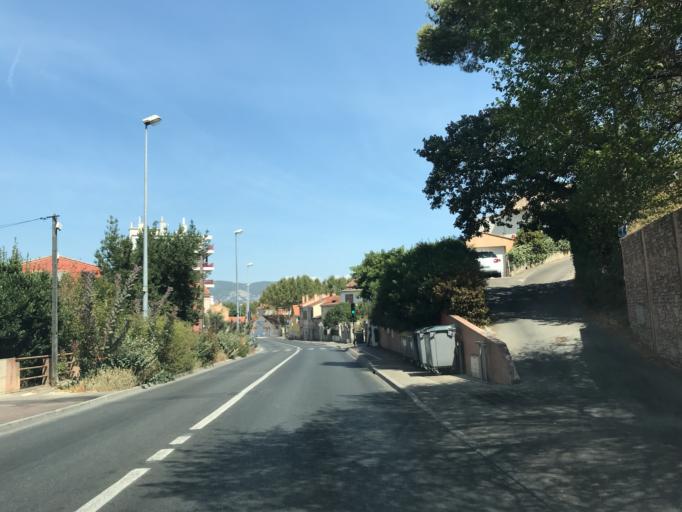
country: FR
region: Provence-Alpes-Cote d'Azur
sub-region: Departement du Var
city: La Seyne-sur-Mer
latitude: 43.0934
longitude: 5.8813
